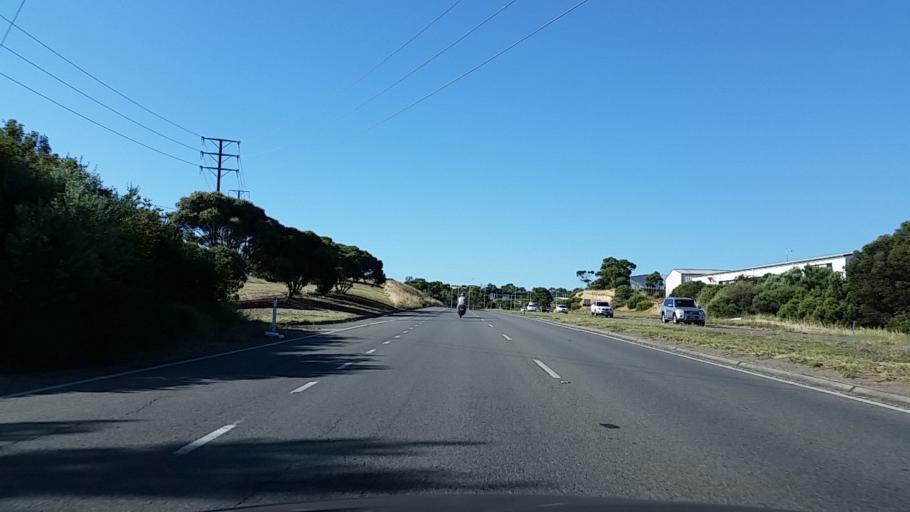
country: AU
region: South Australia
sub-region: Onkaparinga
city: Morphett Vale
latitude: -35.1162
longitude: 138.4908
